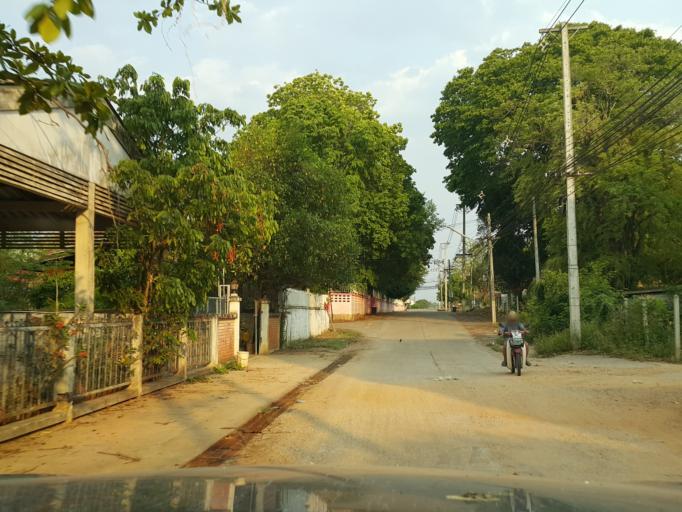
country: TH
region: Lamphun
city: Li
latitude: 17.8043
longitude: 98.9493
